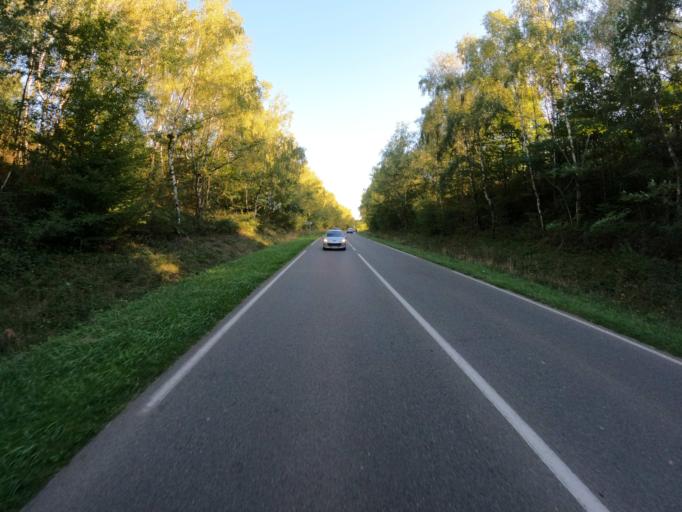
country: FR
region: Bourgogne
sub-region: Departement de Saone-et-Loire
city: Torcy
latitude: 46.7441
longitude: 4.4442
